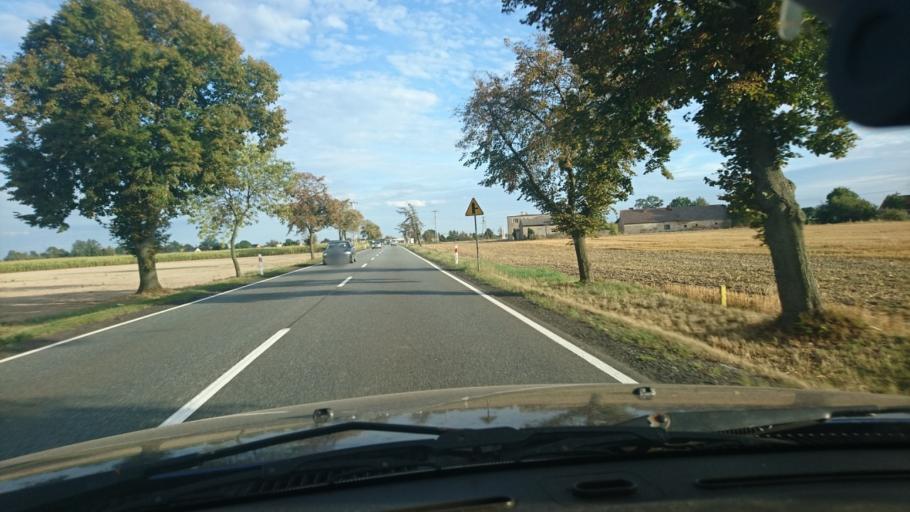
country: PL
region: Opole Voivodeship
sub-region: Powiat kluczborski
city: Kluczbork
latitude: 51.0135
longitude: 18.2017
